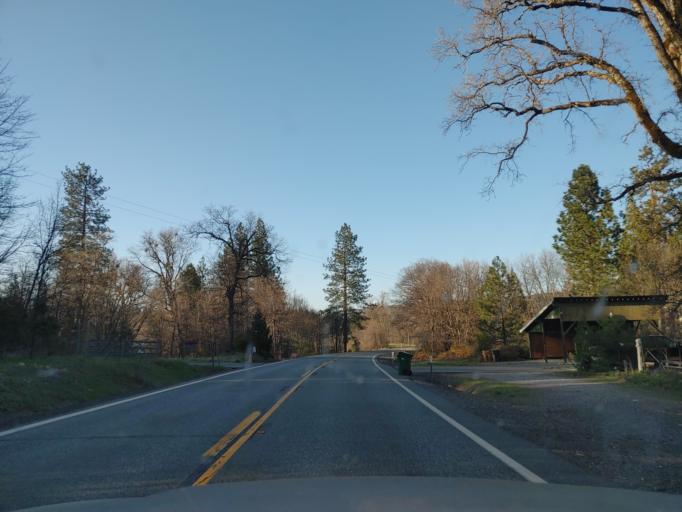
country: US
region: California
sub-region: Shasta County
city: Burney
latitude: 40.8132
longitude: -121.9388
